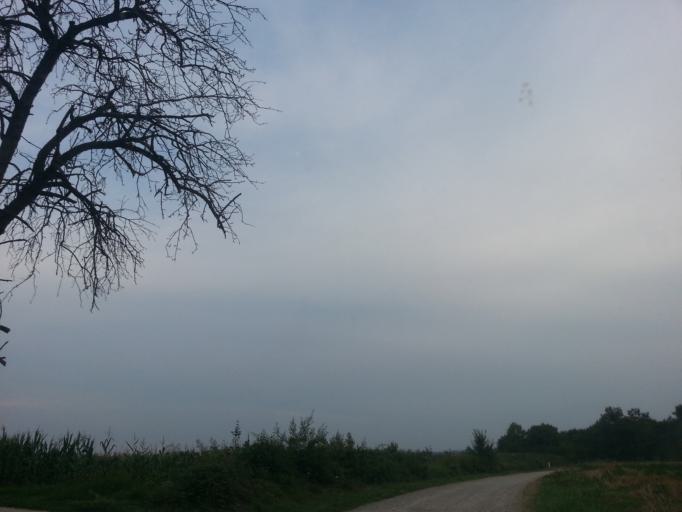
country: BA
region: Brcko
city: Brcko
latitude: 44.7724
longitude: 18.8362
